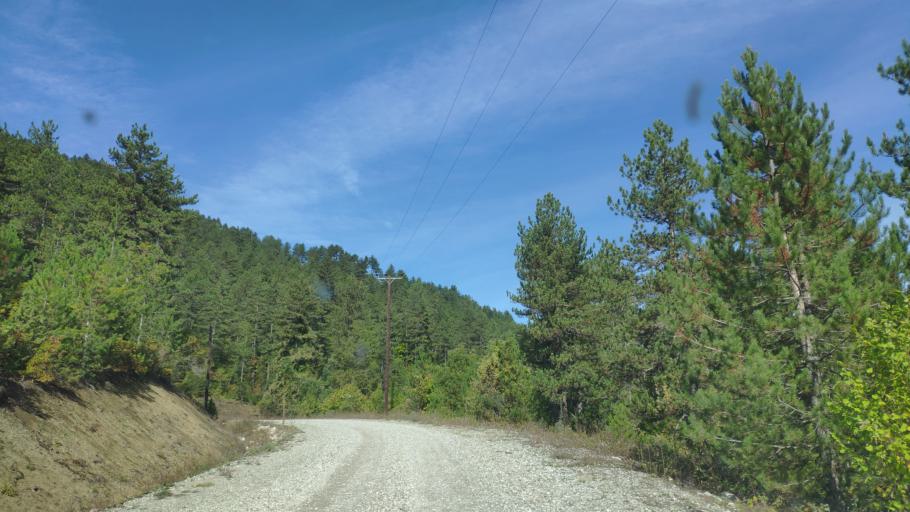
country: AL
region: Korce
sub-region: Rrethi i Devollit
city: Miras
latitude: 40.4141
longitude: 20.8721
